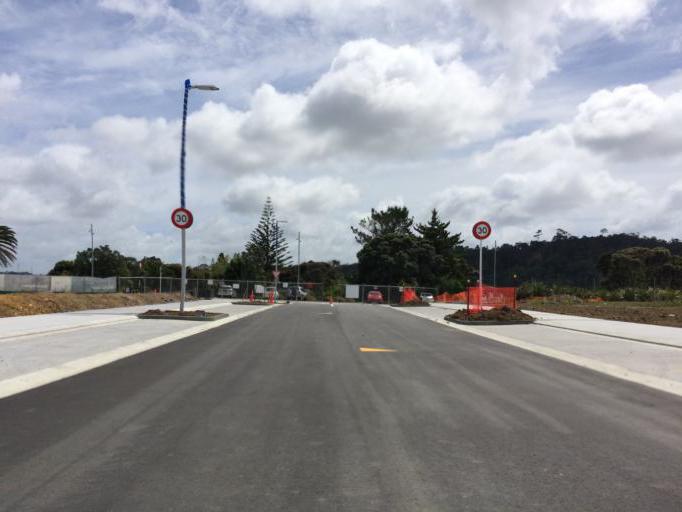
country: NZ
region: Auckland
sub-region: Auckland
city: North Shore
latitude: -36.7901
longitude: 174.6705
